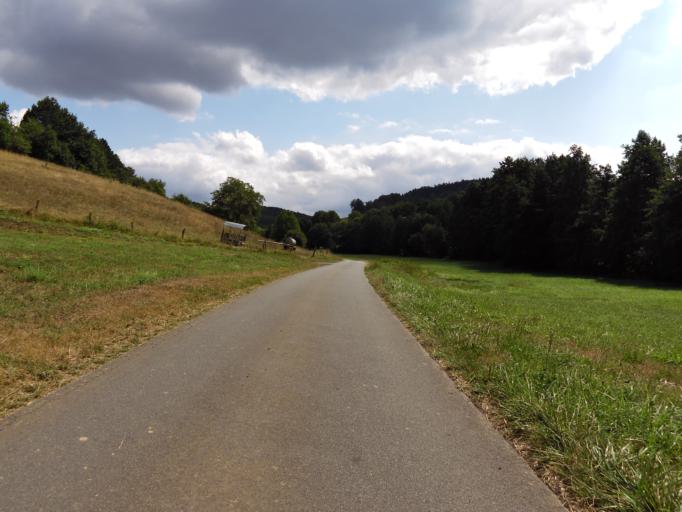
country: DE
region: Hesse
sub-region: Regierungsbezirk Darmstadt
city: Brensbach
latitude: 49.7649
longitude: 8.9011
